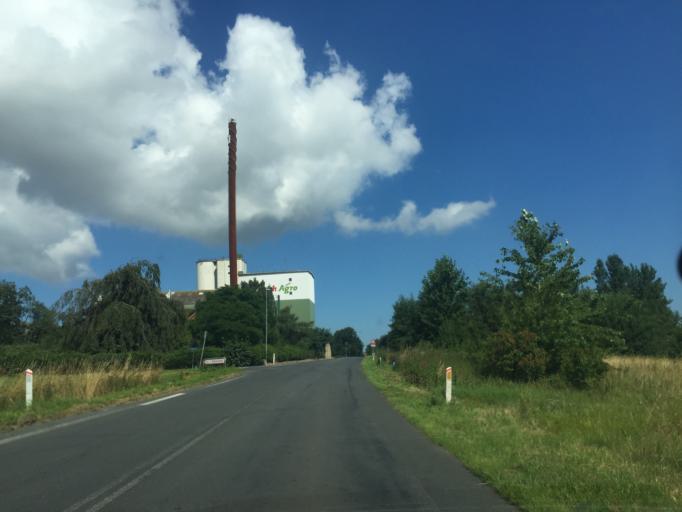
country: DK
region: South Denmark
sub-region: Nordfyns Kommune
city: Otterup
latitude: 55.5343
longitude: 10.3859
